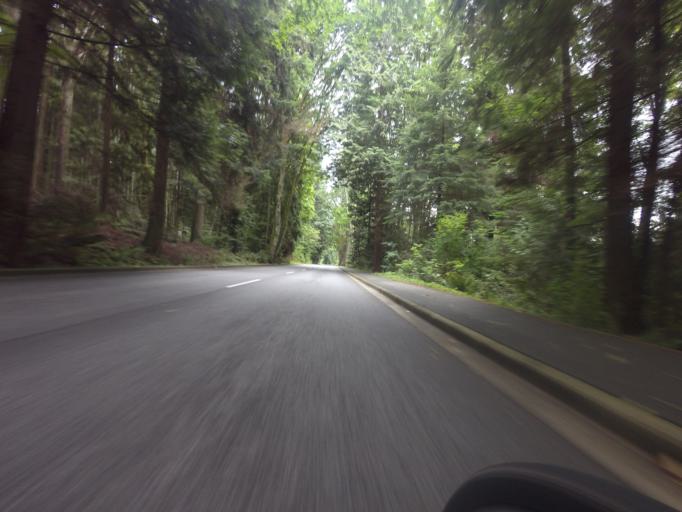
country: CA
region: British Columbia
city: West End
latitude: 49.3059
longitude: -123.1538
